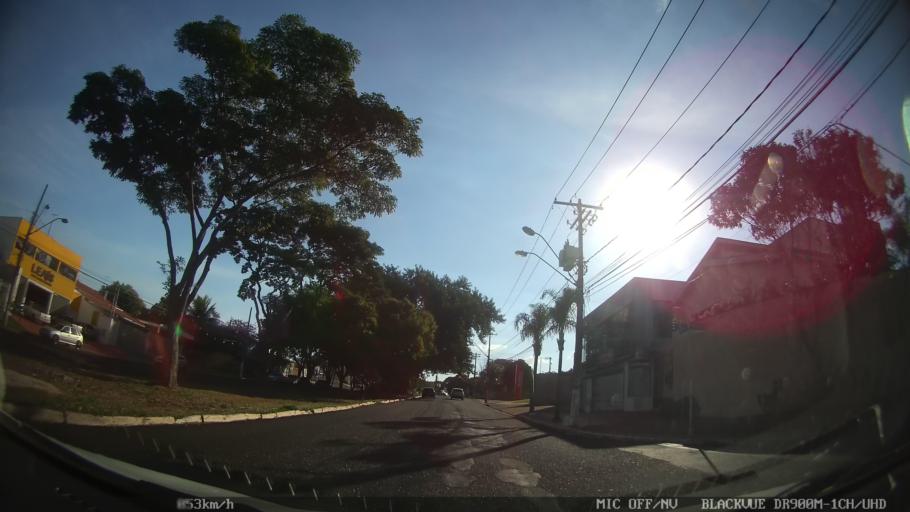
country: BR
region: Sao Paulo
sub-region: Ribeirao Preto
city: Ribeirao Preto
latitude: -21.2040
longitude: -47.7766
